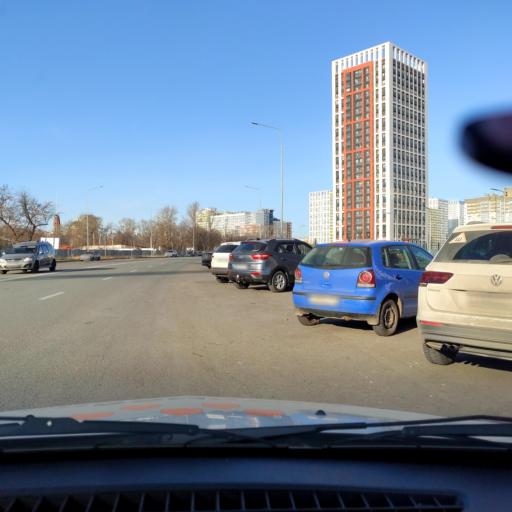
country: RU
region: Bashkortostan
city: Ufa
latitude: 54.7587
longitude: 56.0305
